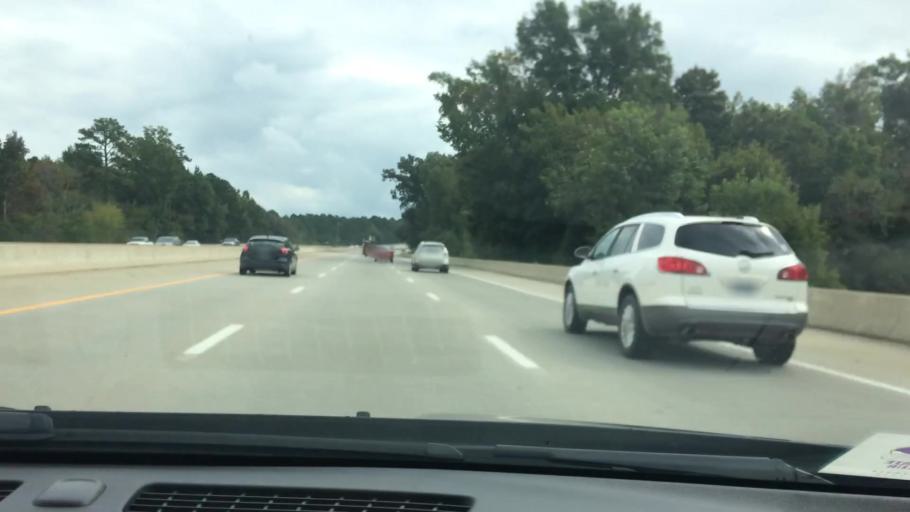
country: US
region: North Carolina
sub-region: Wake County
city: Knightdale
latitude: 35.7728
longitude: -78.5394
